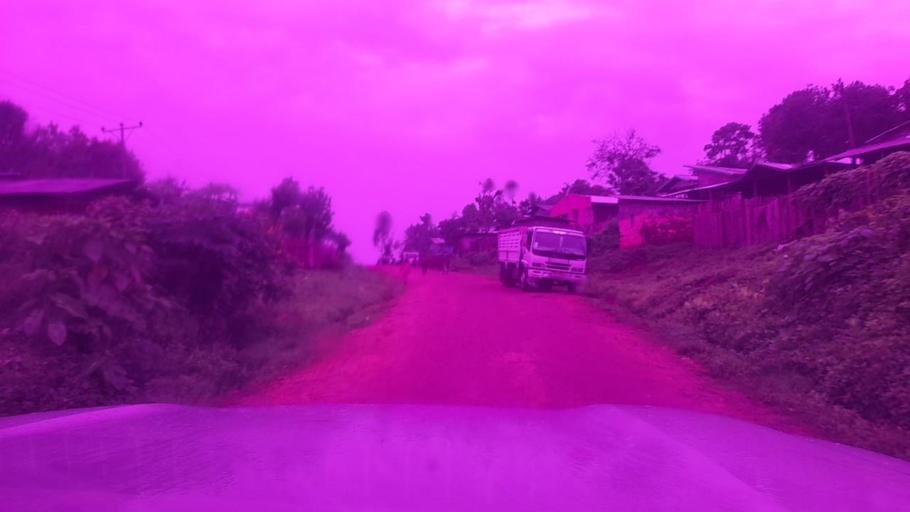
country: ET
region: Southern Nations, Nationalities, and People's Region
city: Bonga
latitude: 7.4402
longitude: 36.1658
